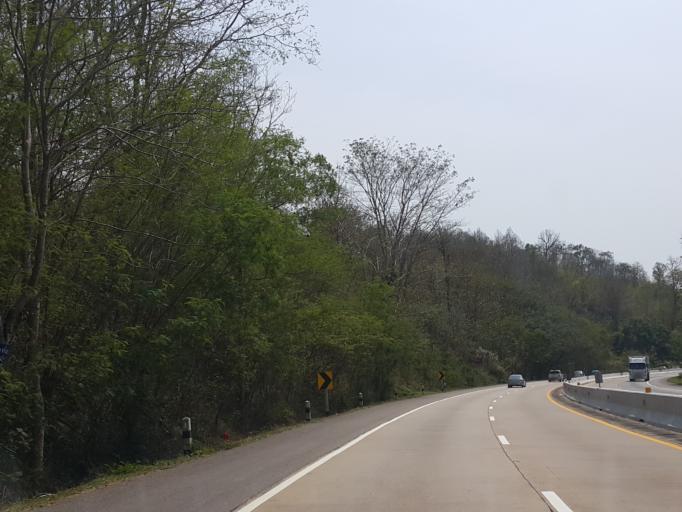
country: TH
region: Lampang
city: Hang Chat
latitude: 18.3447
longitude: 99.2457
